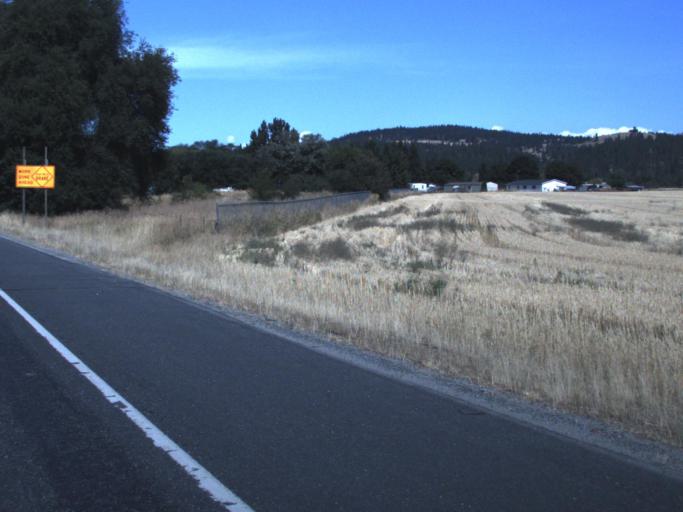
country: US
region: Washington
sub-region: Stevens County
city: Colville
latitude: 48.4495
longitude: -117.8736
